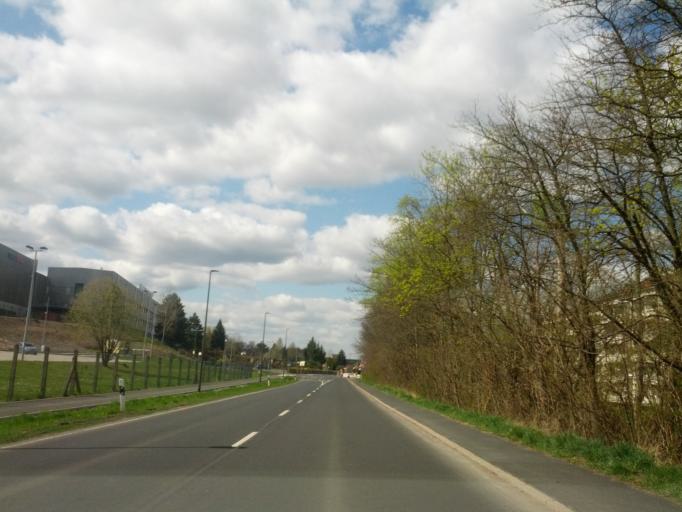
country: DE
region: Thuringia
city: Seebach
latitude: 50.9106
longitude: 10.4283
